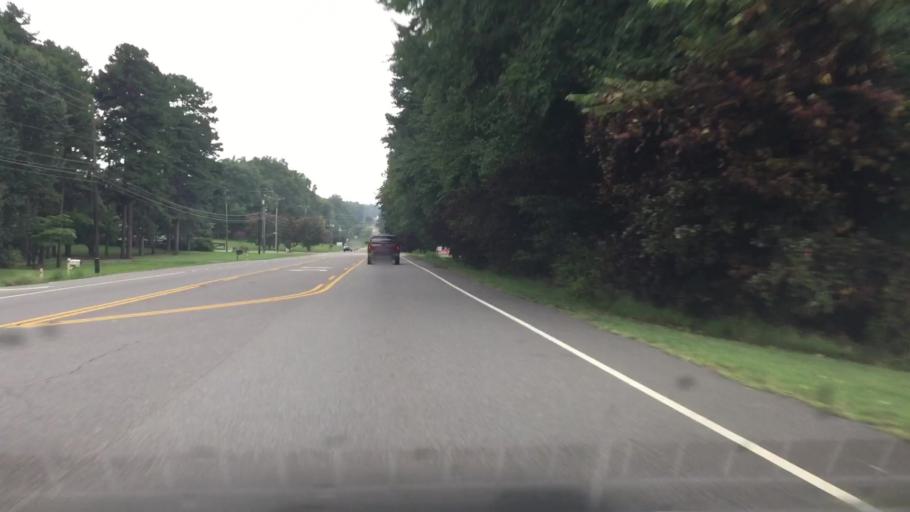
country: US
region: North Carolina
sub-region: Iredell County
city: Mooresville
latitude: 35.5738
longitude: -80.8432
